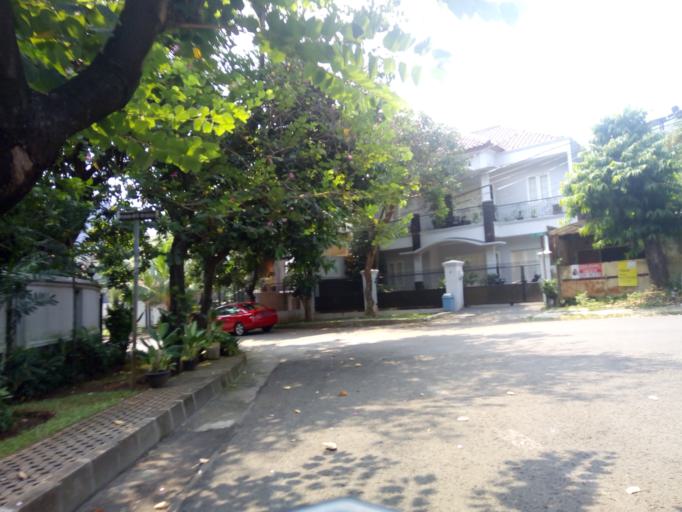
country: ID
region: Jakarta Raya
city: Jakarta
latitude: -6.2370
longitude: 106.7914
